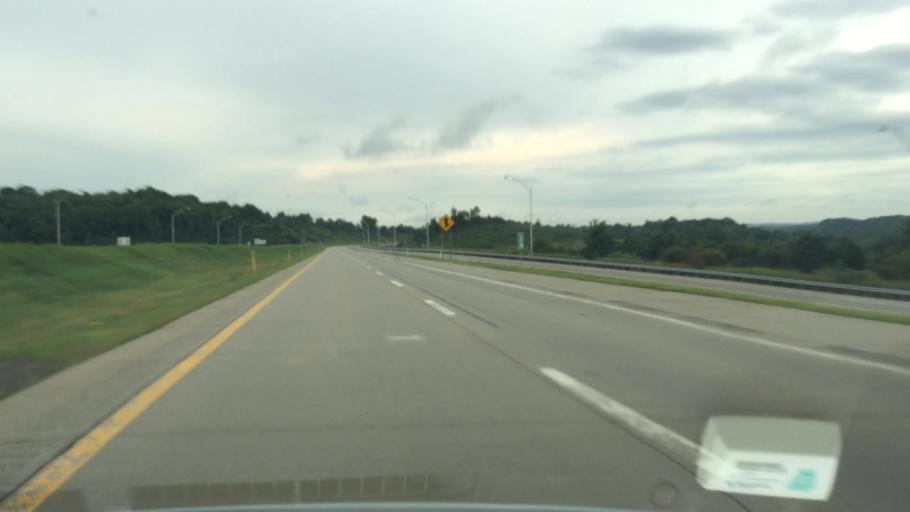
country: US
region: Pennsylvania
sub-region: Allegheny County
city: Imperial
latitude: 40.4474
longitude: -80.3085
